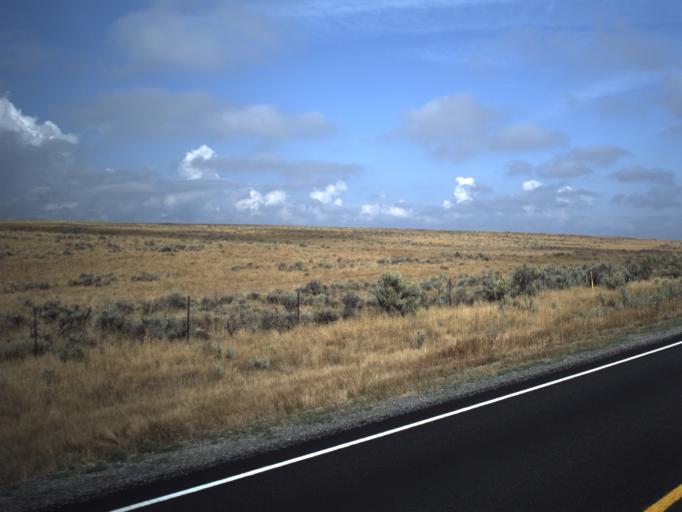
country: US
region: Utah
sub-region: Rich County
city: Randolph
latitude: 41.5502
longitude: -111.1551
